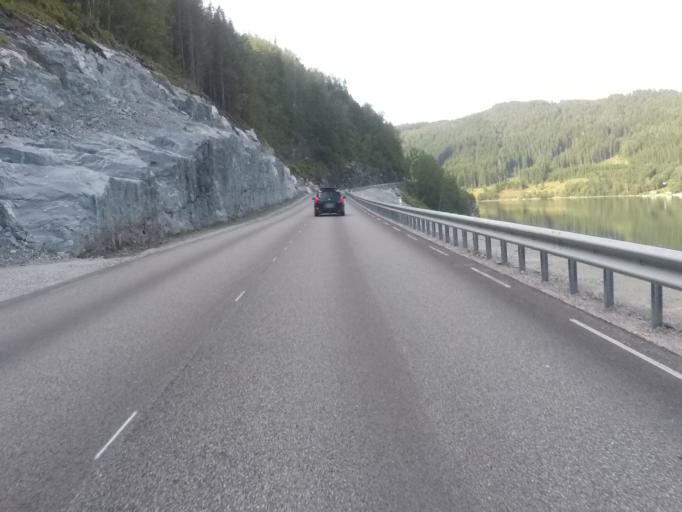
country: NO
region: More og Romsdal
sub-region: Rauma
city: Andalsnes
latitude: 62.5802
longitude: 7.5437
